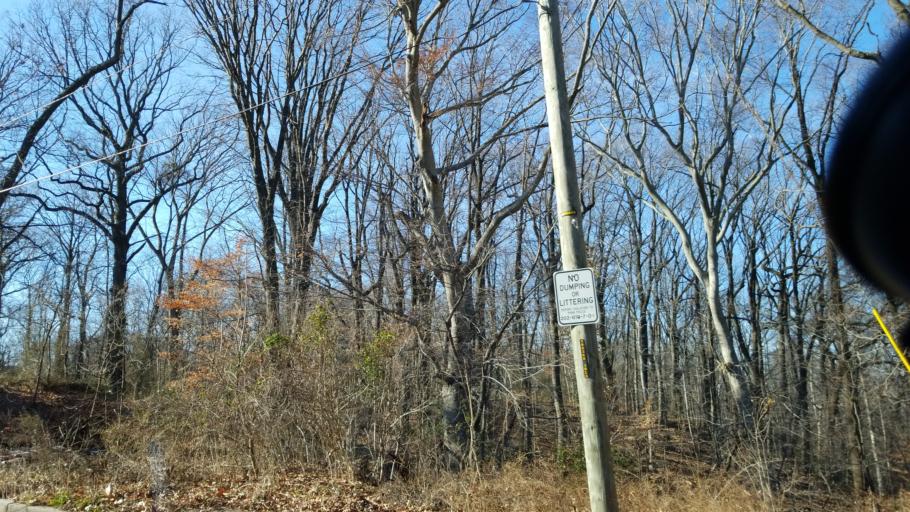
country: US
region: Maryland
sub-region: Prince George's County
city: Glassmanor
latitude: 38.8447
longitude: -77.0020
